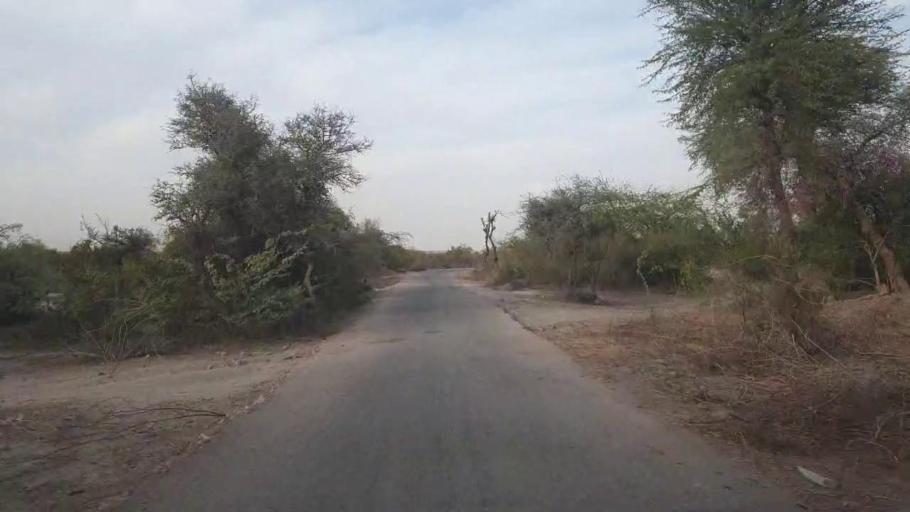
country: PK
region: Sindh
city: Nabisar
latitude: 25.1108
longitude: 69.6779
